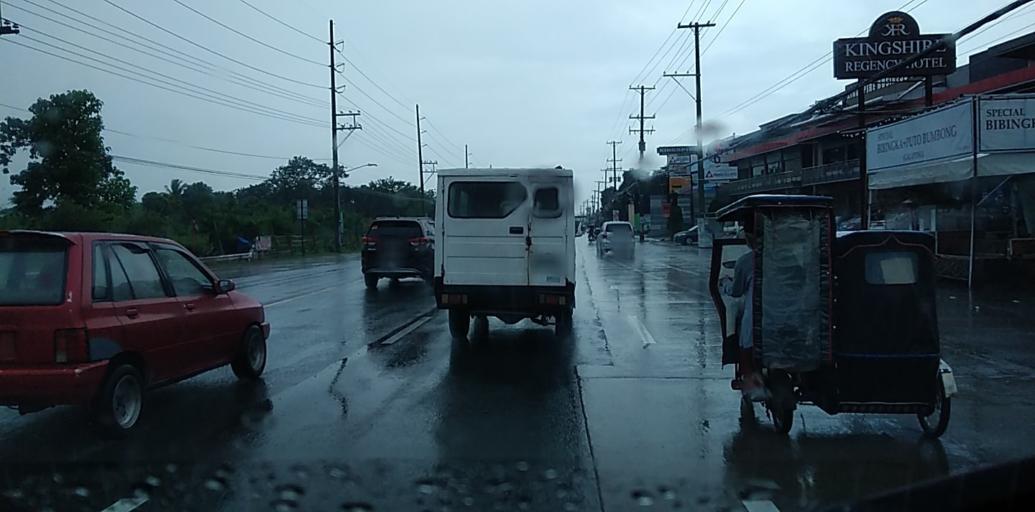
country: PH
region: Central Luzon
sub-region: Province of Pampanga
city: Bulaon
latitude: 15.0591
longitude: 120.6568
